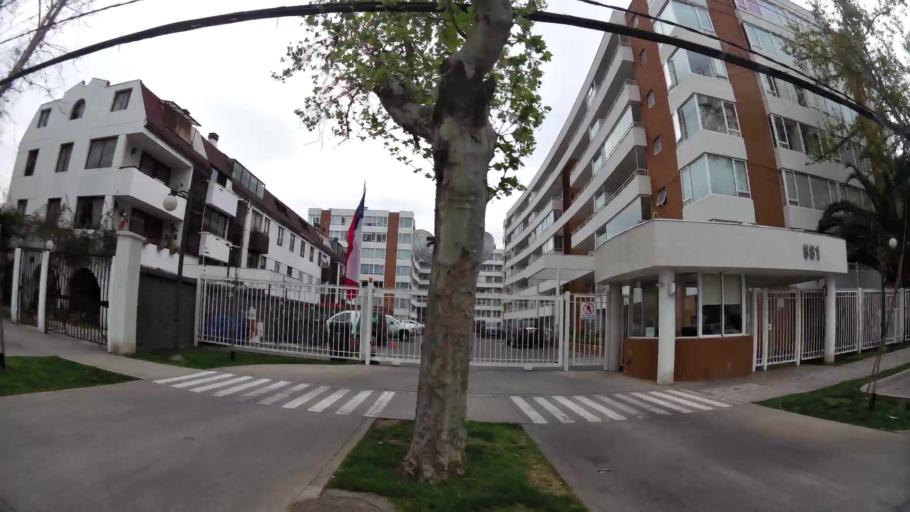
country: CL
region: Santiago Metropolitan
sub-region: Provincia de Santiago
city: Villa Presidente Frei, Nunoa, Santiago, Chile
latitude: -33.4631
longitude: -70.6002
